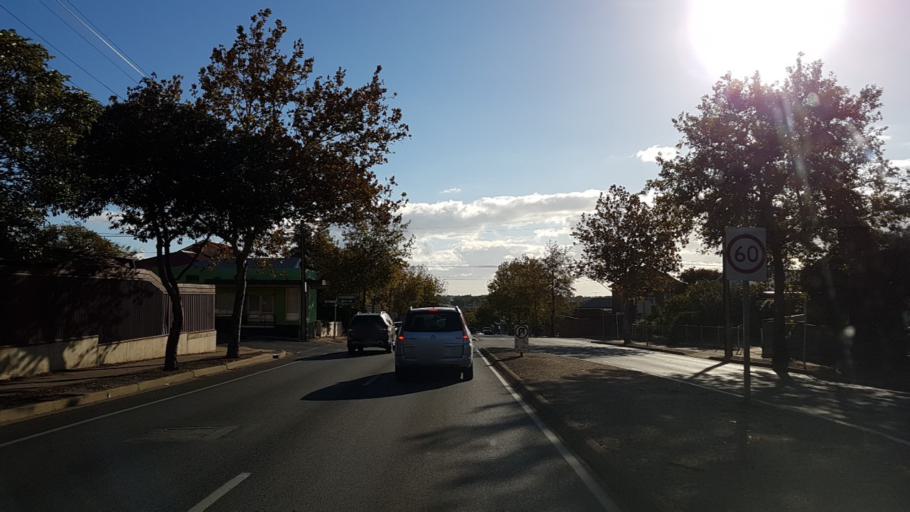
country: AU
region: South Australia
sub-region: Prospect
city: Prospect
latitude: -34.8741
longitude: 138.5951
